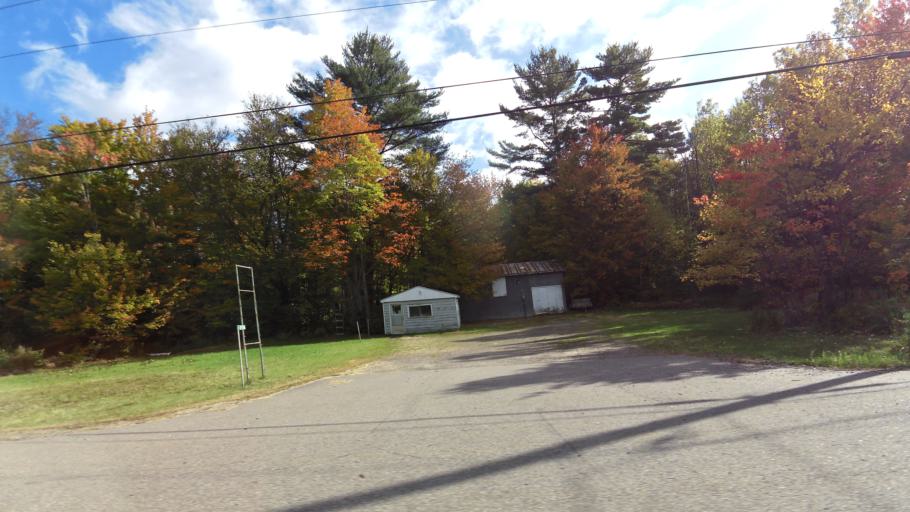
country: CA
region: Ontario
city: Deep River
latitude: 46.0726
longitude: -77.4760
